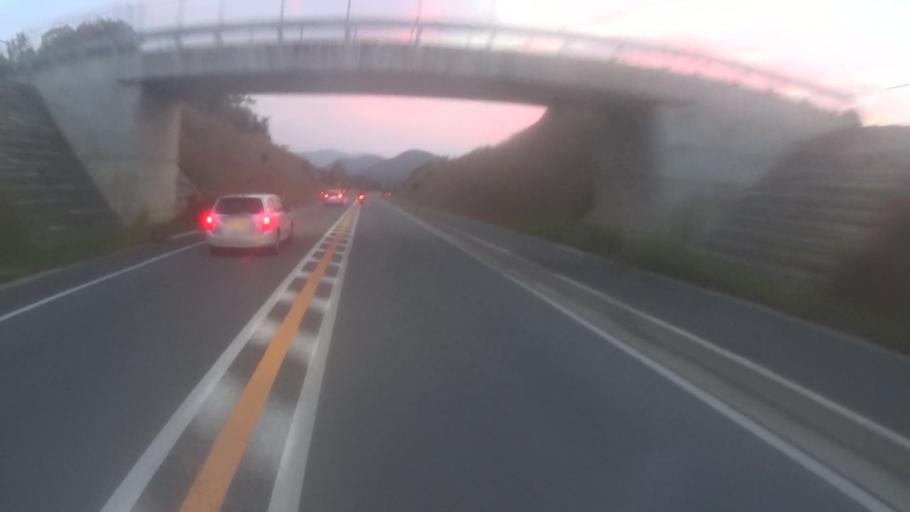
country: JP
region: Kyoto
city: Ayabe
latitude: 35.2024
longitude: 135.4300
